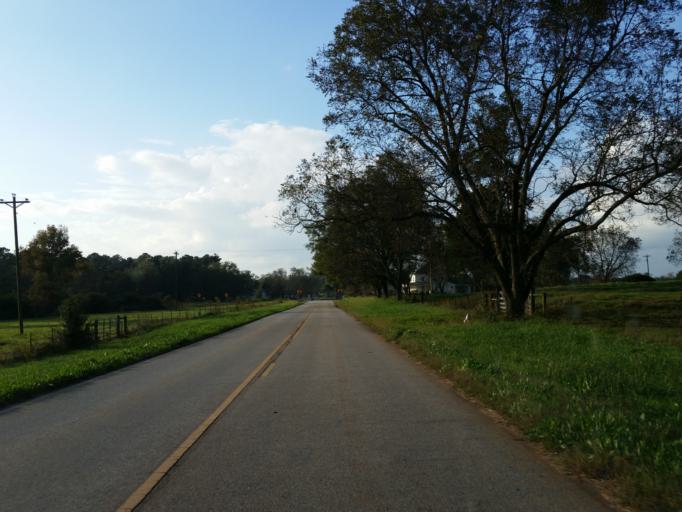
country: US
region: Georgia
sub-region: Monroe County
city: Forsyth
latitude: 32.9800
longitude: -83.8741
